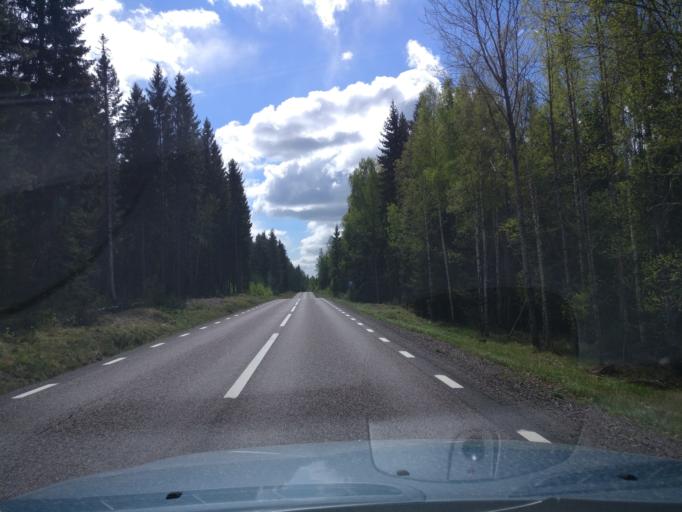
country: SE
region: Vaermland
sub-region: Karlstads Kommun
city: Molkom
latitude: 59.7319
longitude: 13.6795
